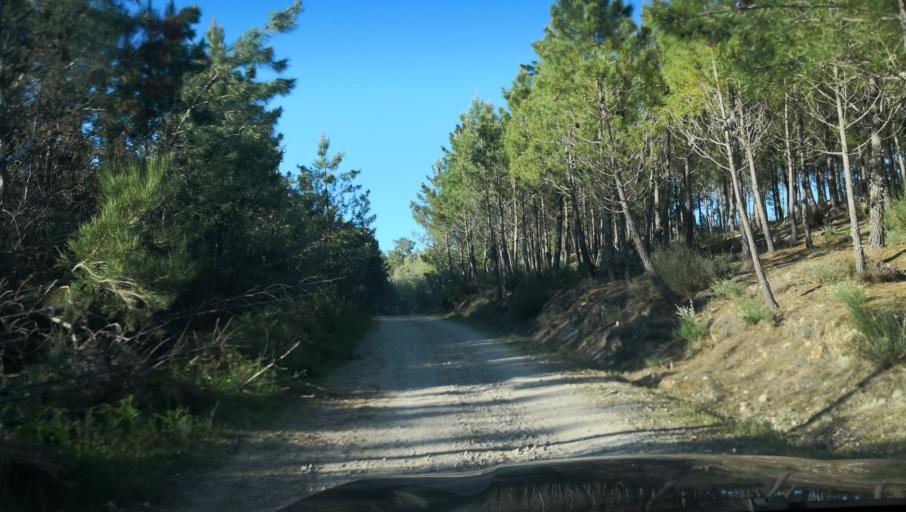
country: PT
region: Vila Real
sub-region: Vila Real
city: Vila Real
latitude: 41.3345
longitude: -7.6720
